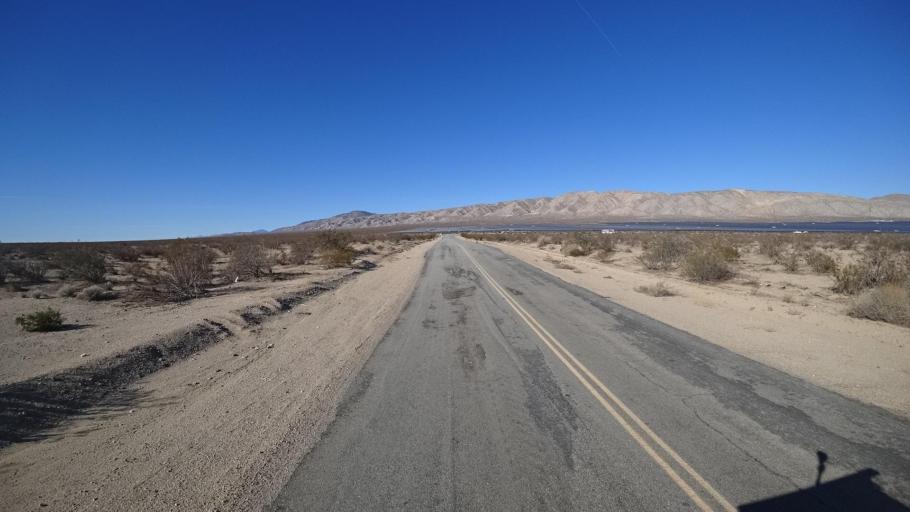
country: US
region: California
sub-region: Kern County
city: California City
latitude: 35.2010
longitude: -118.0665
